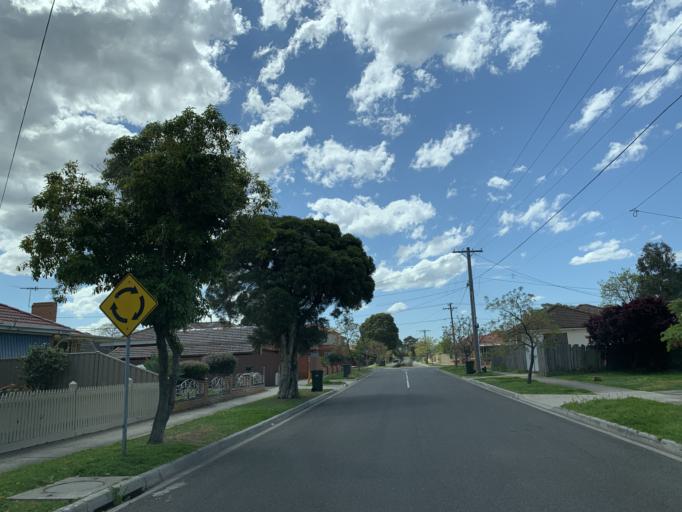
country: AU
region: Victoria
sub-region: Brimbank
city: Albion
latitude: -37.7612
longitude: 144.8285
